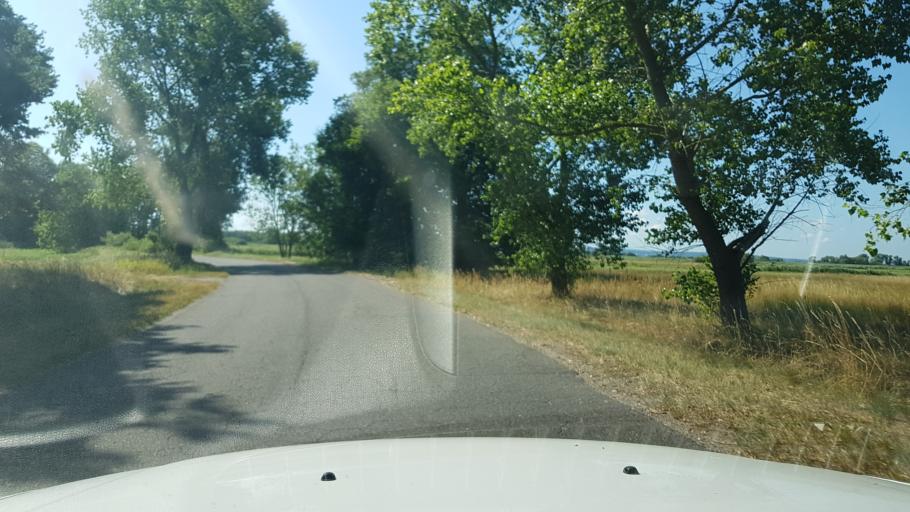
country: PL
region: West Pomeranian Voivodeship
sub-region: Powiat goleniowski
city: Goleniow
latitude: 53.4795
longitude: 14.7103
